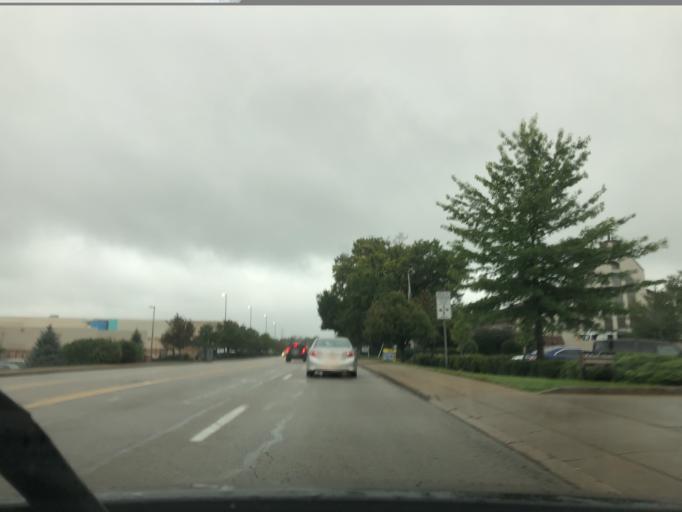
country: US
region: Ohio
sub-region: Hamilton County
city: Rossmoyne
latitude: 39.2025
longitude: -84.3801
